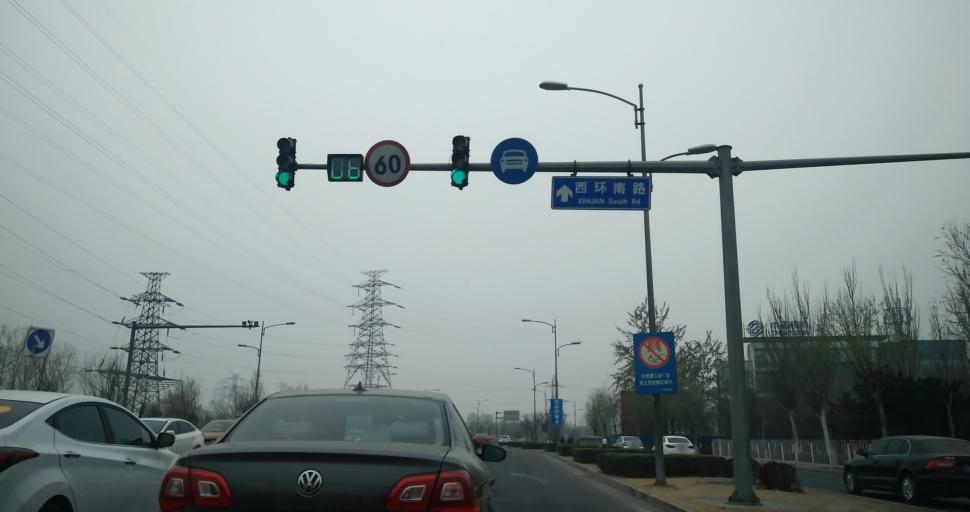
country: CN
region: Beijing
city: Qingyundian
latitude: 39.7632
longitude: 116.5366
